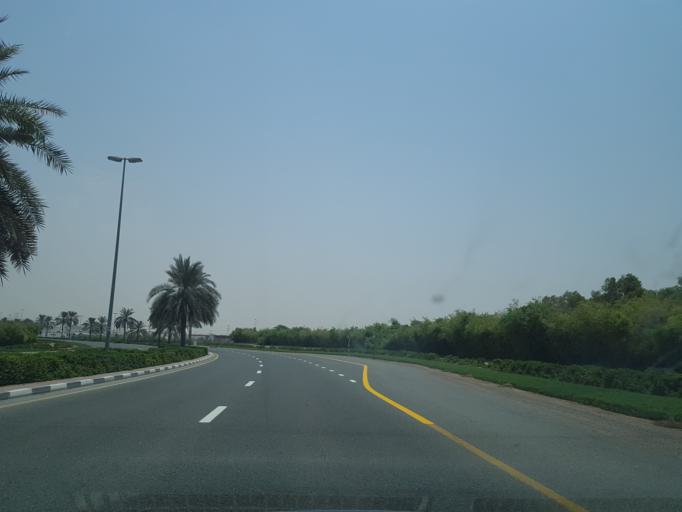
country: AE
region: Ash Shariqah
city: Sharjah
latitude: 25.1110
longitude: 55.3954
